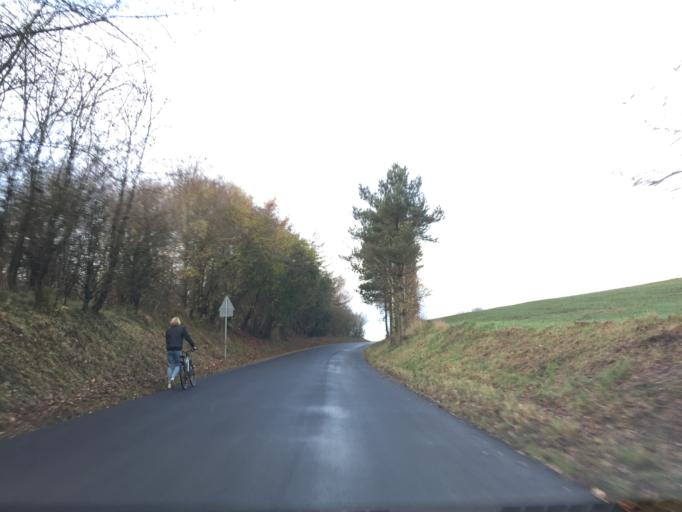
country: DK
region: Central Jutland
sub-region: Silkeborg Kommune
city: Svejbaek
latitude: 56.1605
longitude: 9.6921
